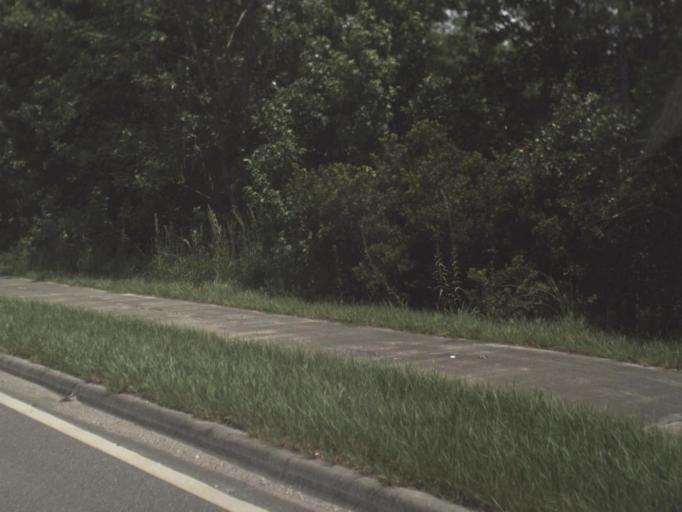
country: US
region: Florida
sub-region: Pinellas County
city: Saint George
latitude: 28.0279
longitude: -82.7088
